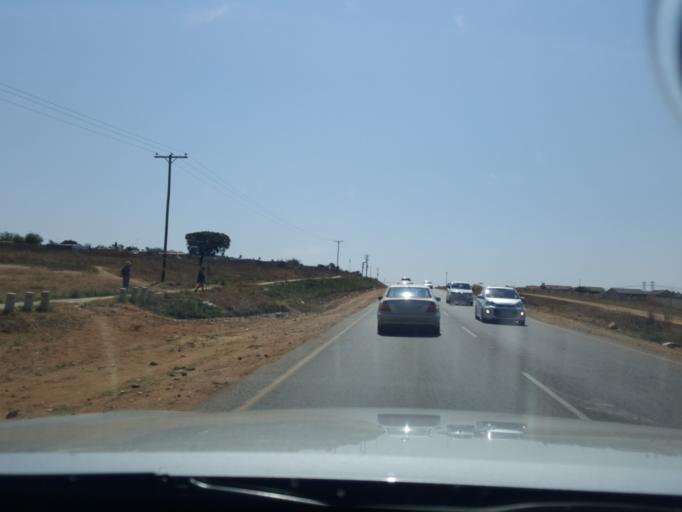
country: ZA
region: Gauteng
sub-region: City of Johannesburg Metropolitan Municipality
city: Midrand
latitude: -25.9148
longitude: 28.1002
